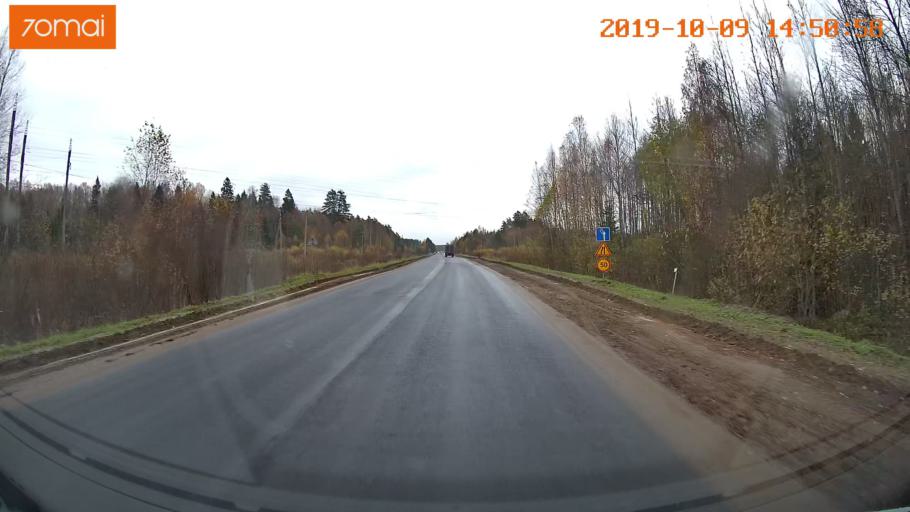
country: RU
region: Kostroma
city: Chistyye Bory
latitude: 58.3801
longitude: 41.6082
